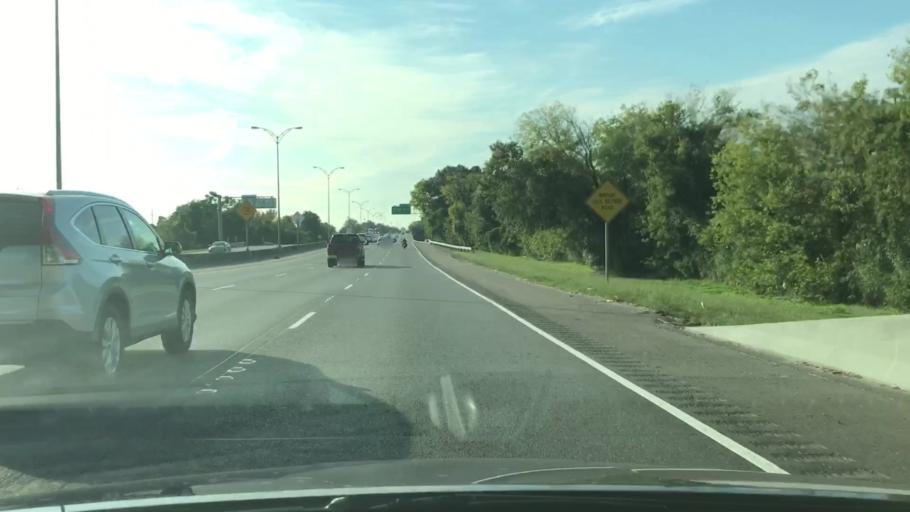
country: US
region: Louisiana
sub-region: Orleans Parish
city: New Orleans
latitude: 29.9932
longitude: -90.0870
